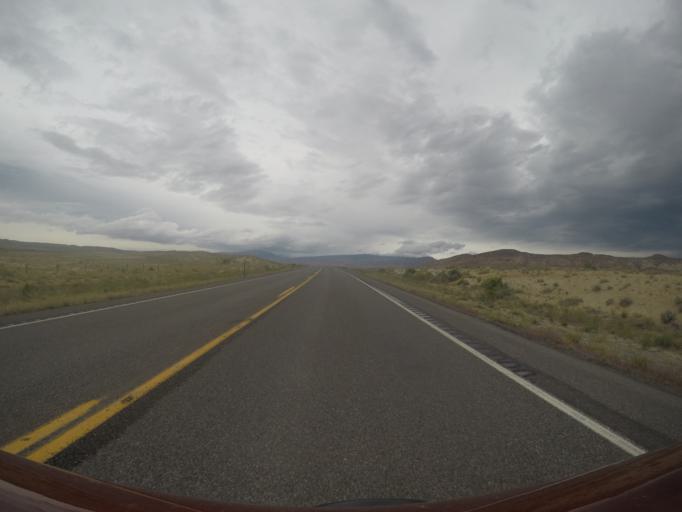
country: US
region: Wyoming
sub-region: Big Horn County
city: Lovell
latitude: 44.9141
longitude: -108.2924
